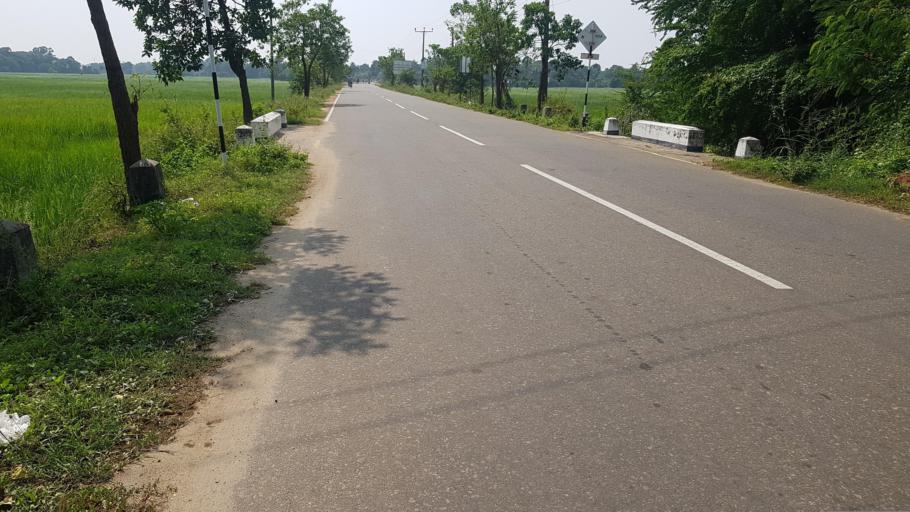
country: LK
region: Northern Province
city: Jaffna
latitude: 9.7283
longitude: 79.9485
